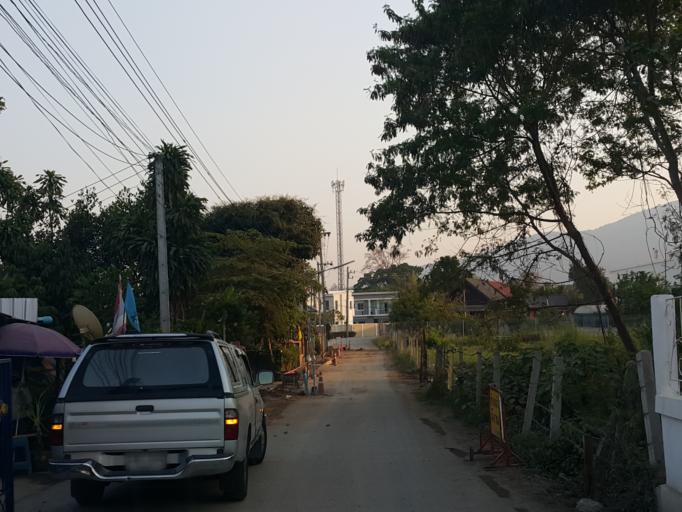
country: TH
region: Chiang Mai
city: San Sai
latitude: 18.9003
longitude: 98.9535
